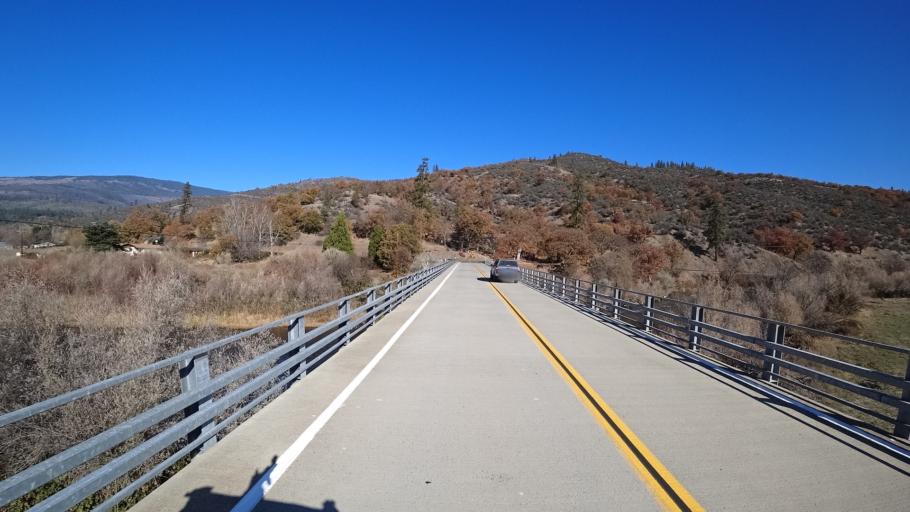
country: US
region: California
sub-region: Siskiyou County
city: Yreka
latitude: 41.8370
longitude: -122.8648
